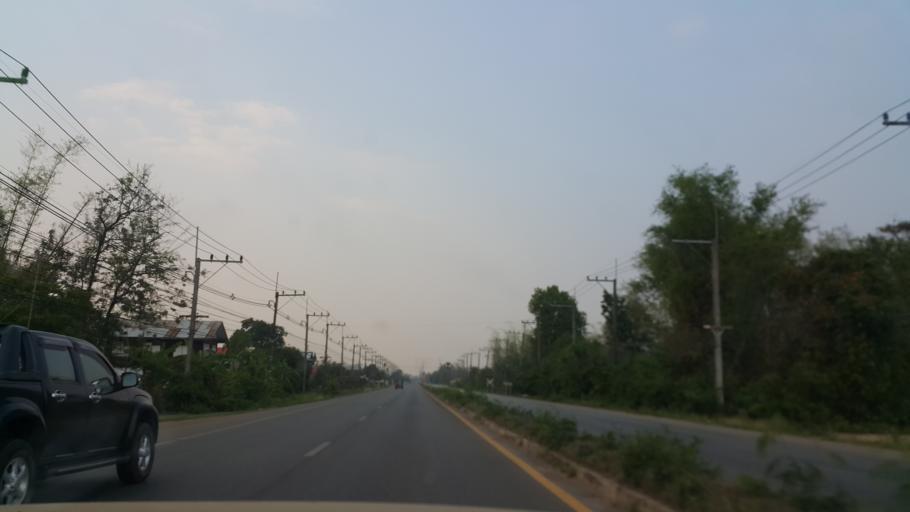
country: TH
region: Nakhon Phanom
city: That Phanom
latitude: 16.9938
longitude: 104.7238
